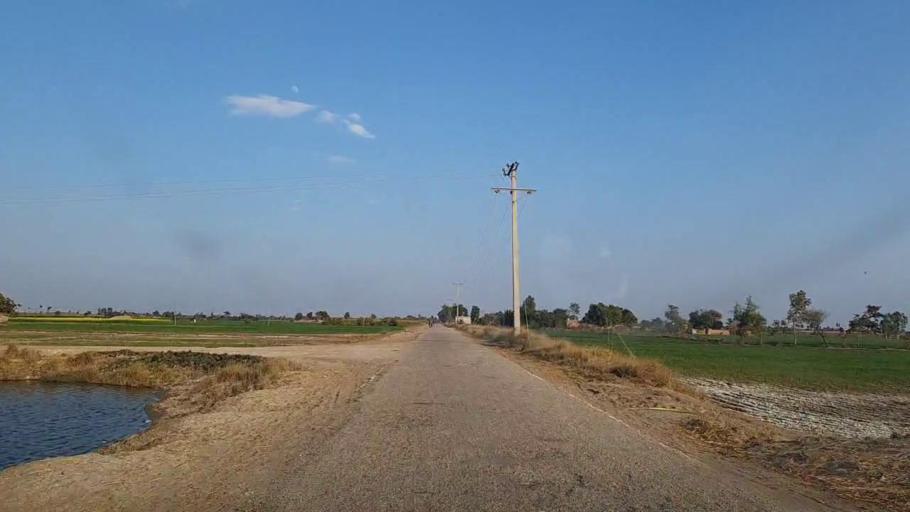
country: PK
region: Sindh
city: Sanghar
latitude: 26.2643
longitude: 68.9538
